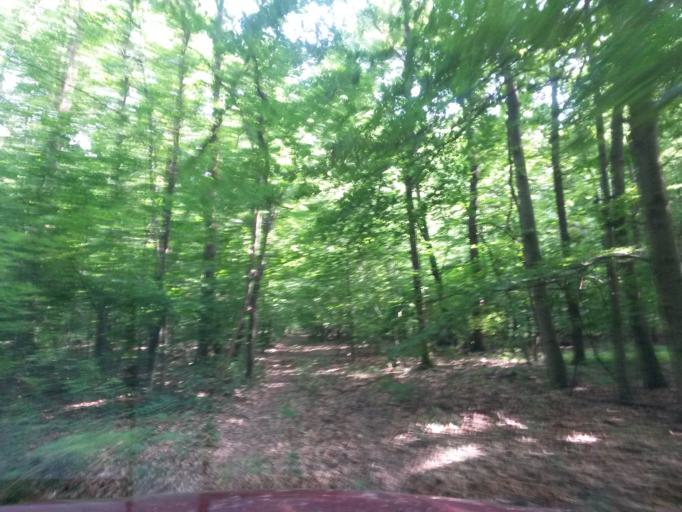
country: SK
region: Kosicky
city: Moldava nad Bodvou
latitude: 48.6177
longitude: 21.1070
